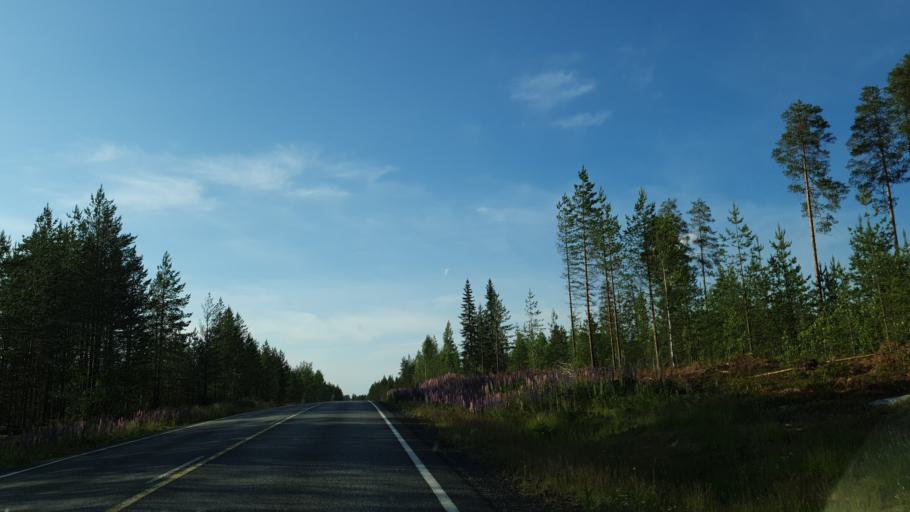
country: FI
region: Kainuu
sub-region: Kehys-Kainuu
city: Kuhmo
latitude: 64.0840
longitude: 29.4842
